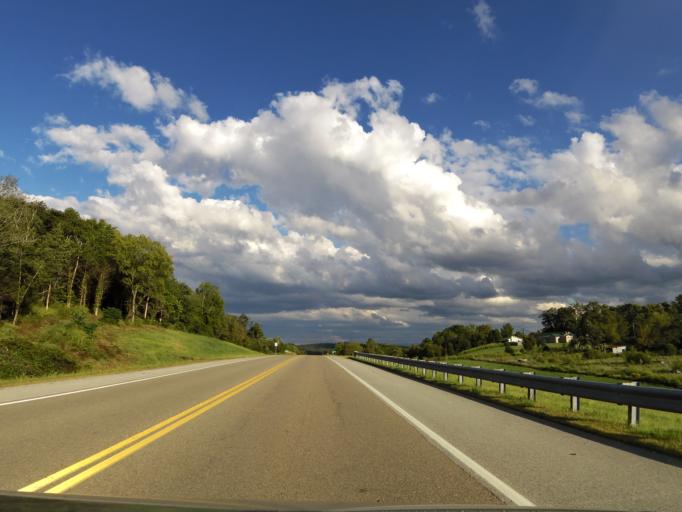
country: US
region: Tennessee
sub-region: Grainger County
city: Blaine
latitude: 36.1609
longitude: -83.7334
